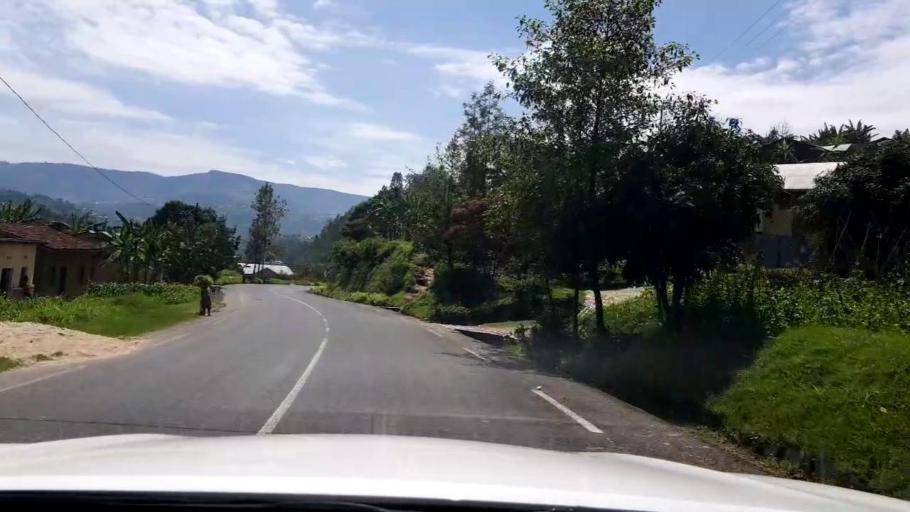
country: RW
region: Southern Province
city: Gitarama
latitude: -1.9206
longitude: 29.6479
